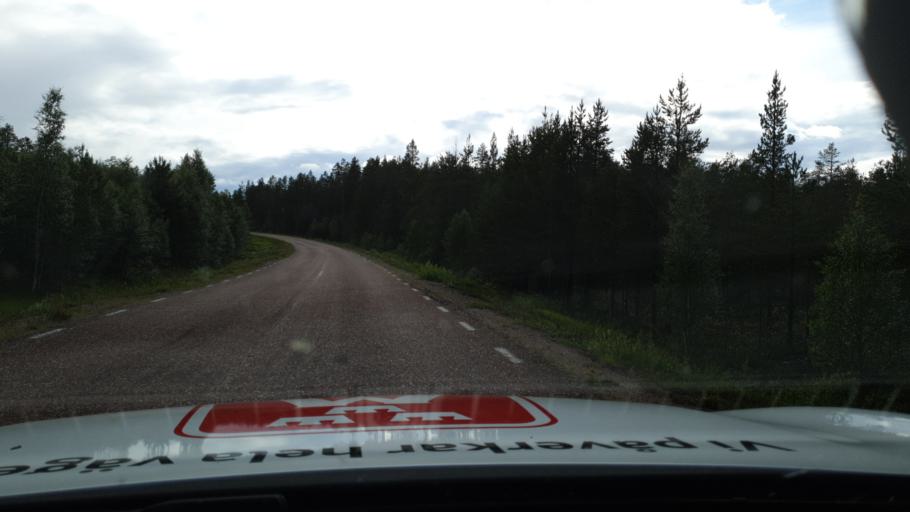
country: SE
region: Dalarna
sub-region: Alvdalens Kommun
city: AElvdalen
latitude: 61.7810
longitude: 13.4849
